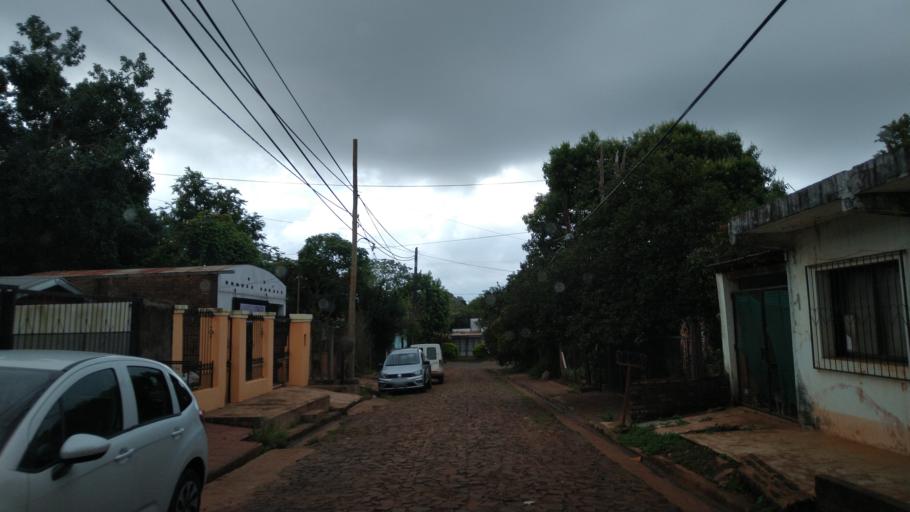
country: AR
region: Misiones
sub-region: Departamento de Capital
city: Posadas
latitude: -27.4111
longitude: -55.9038
